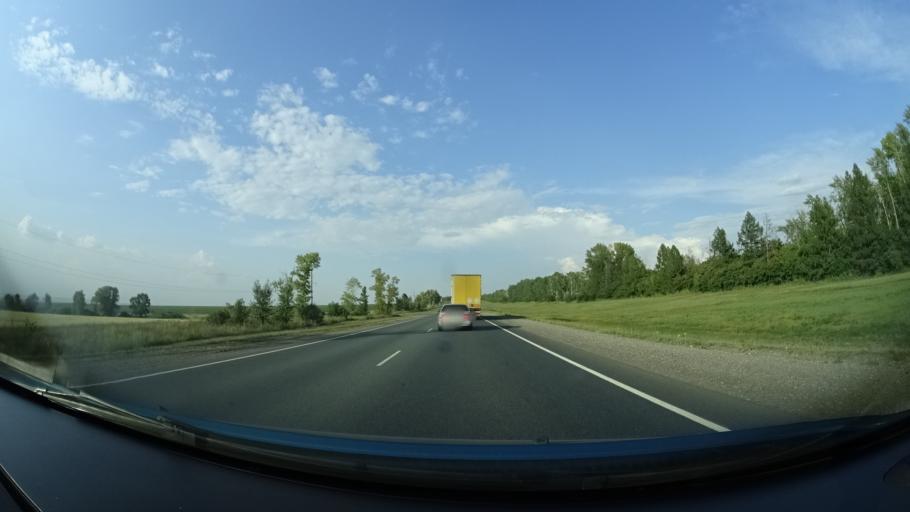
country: RU
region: Samara
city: Krasnyy Yar
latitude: 53.6564
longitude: 50.7491
